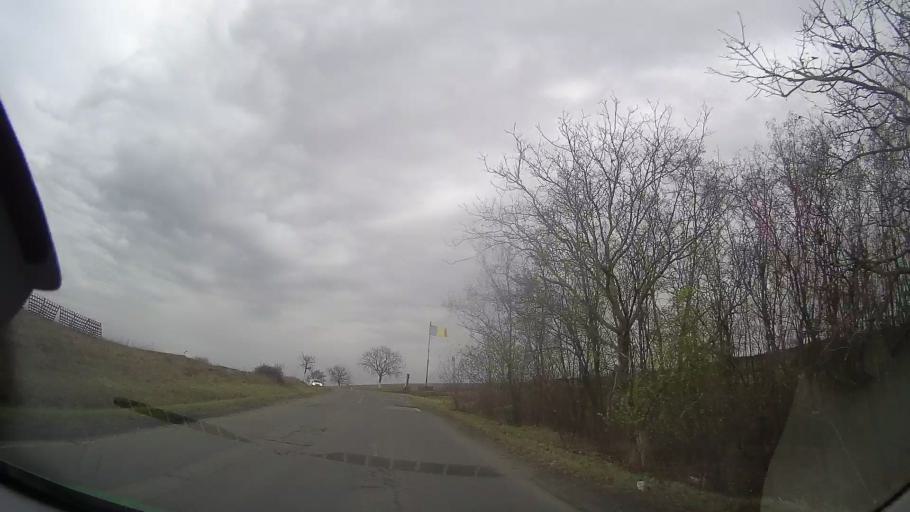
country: RO
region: Mures
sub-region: Comuna Faragau
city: Faragau
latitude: 46.7628
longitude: 24.5295
